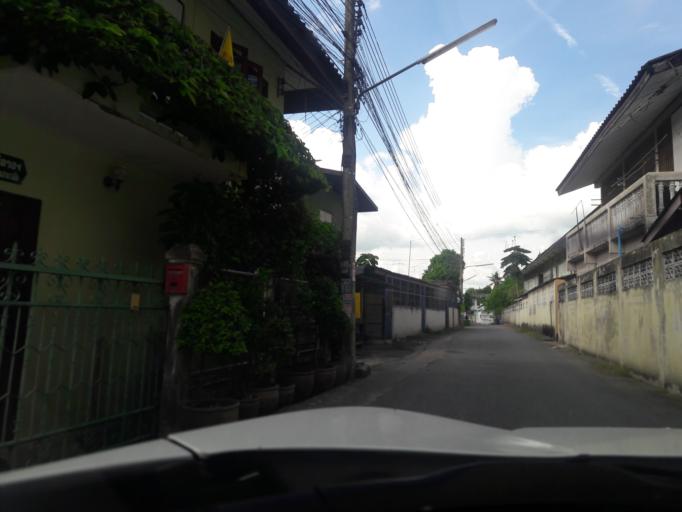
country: TH
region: Lop Buri
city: Ban Mi
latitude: 15.0462
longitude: 100.5377
